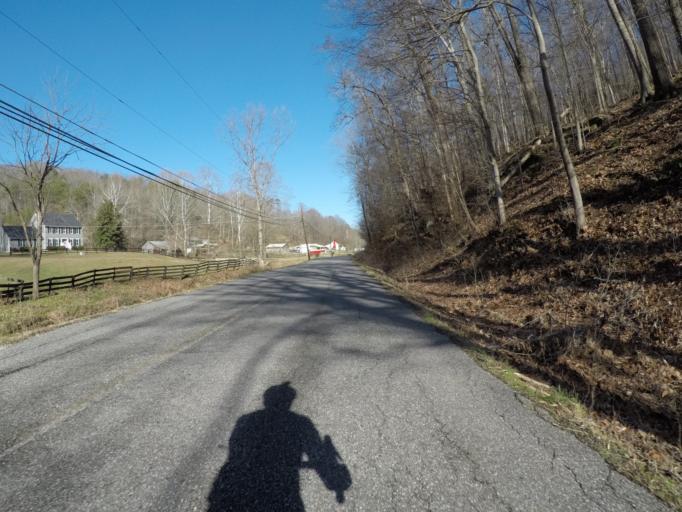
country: US
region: Kentucky
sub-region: Boyd County
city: Catlettsburg
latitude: 38.4234
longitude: -82.6375
